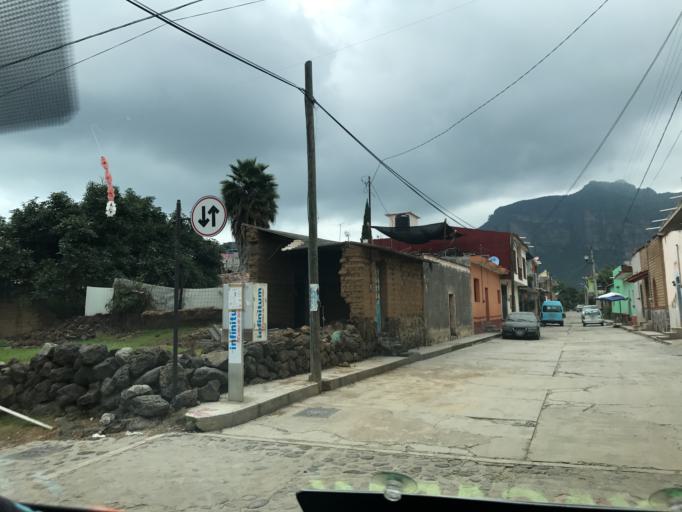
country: MX
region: Morelos
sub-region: Tlayacapan
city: Tlayacapan
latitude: 18.9606
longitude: -98.9833
